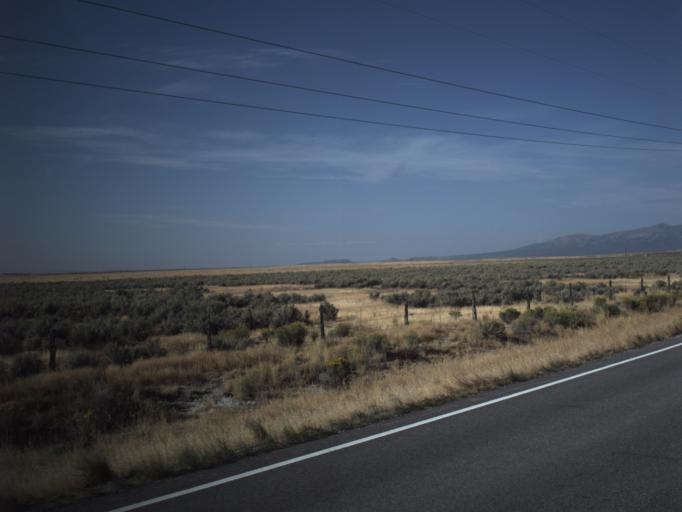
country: US
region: Idaho
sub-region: Oneida County
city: Malad City
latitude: 41.9661
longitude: -112.9707
